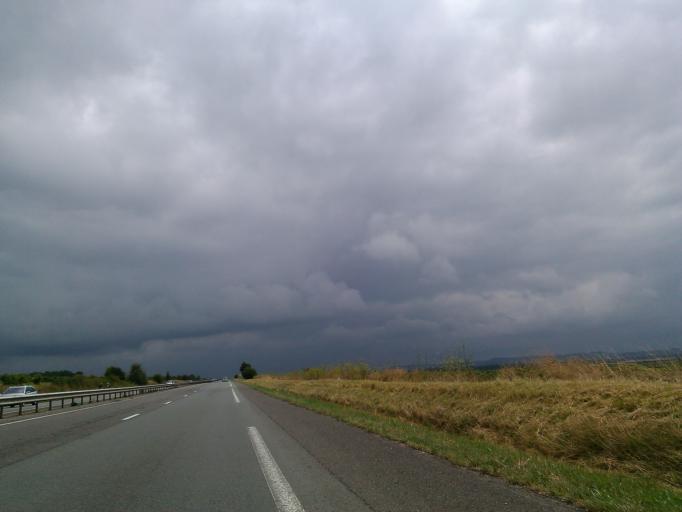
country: FR
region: Poitou-Charentes
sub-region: Departement de la Charente
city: Gensac-la-Pallue
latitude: 45.6693
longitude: -0.2518
